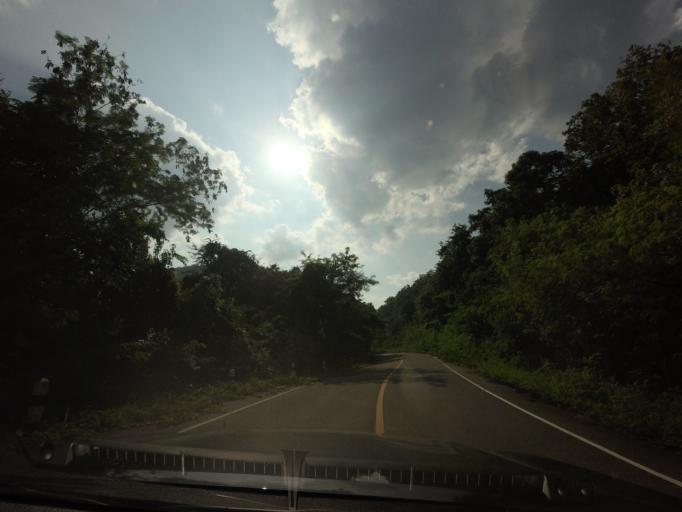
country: TH
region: Nan
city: Na Noi
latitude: 18.3124
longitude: 100.9021
